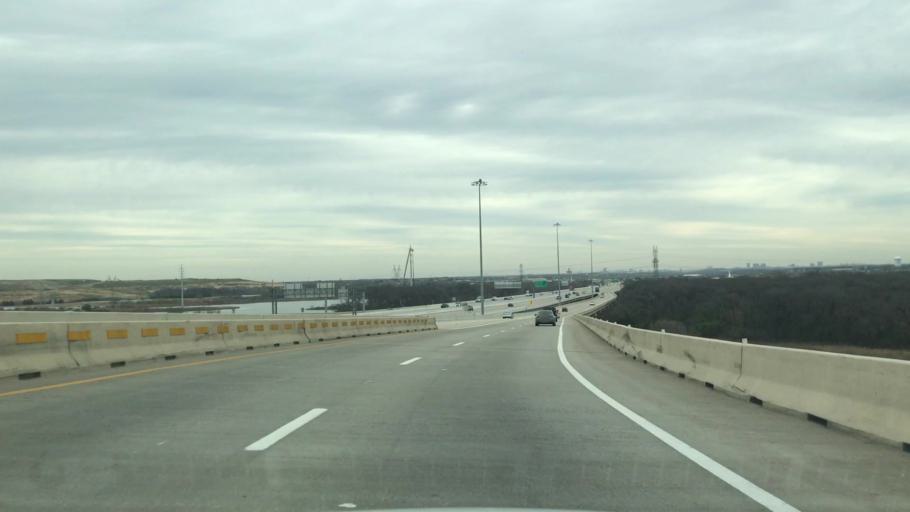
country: US
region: Texas
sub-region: Denton County
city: Lewisville
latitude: 33.0013
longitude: -96.9560
